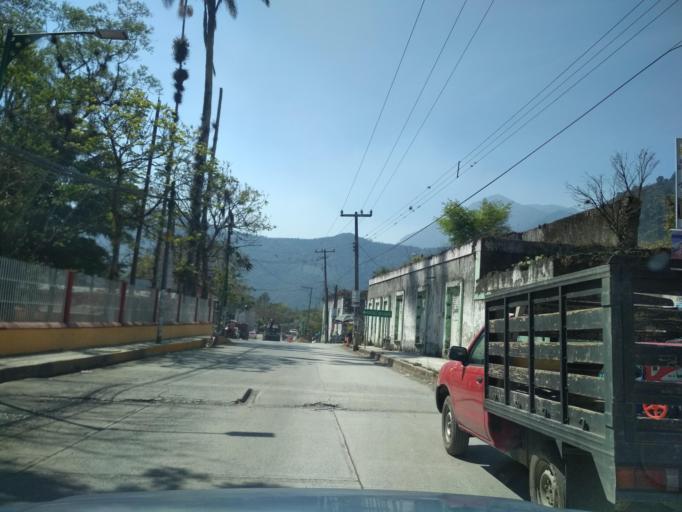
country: MX
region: Veracruz
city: Jalapilla
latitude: 18.8227
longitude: -97.0897
